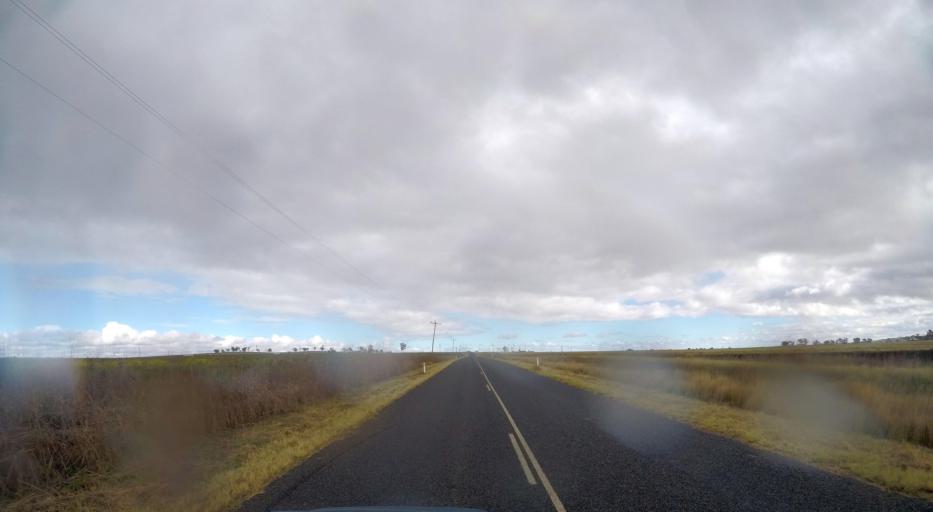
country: AU
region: Queensland
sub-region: Southern Downs
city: Warwick
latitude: -28.0557
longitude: 152.0219
